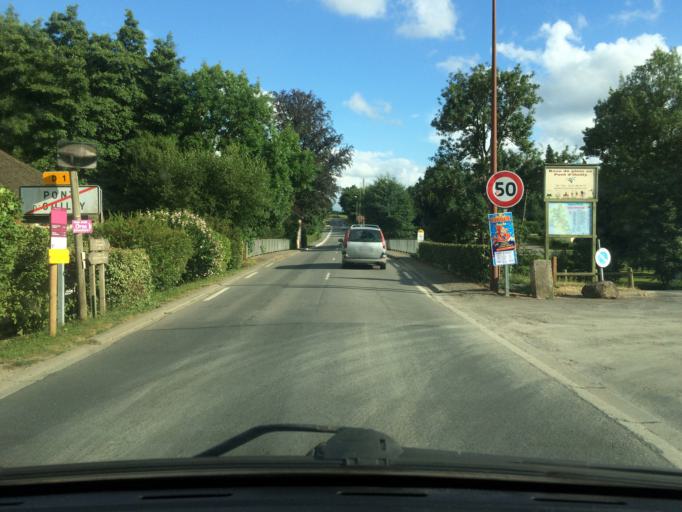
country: FR
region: Lower Normandy
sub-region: Departement du Calvados
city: Clecy
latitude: 48.8710
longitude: -0.4107
